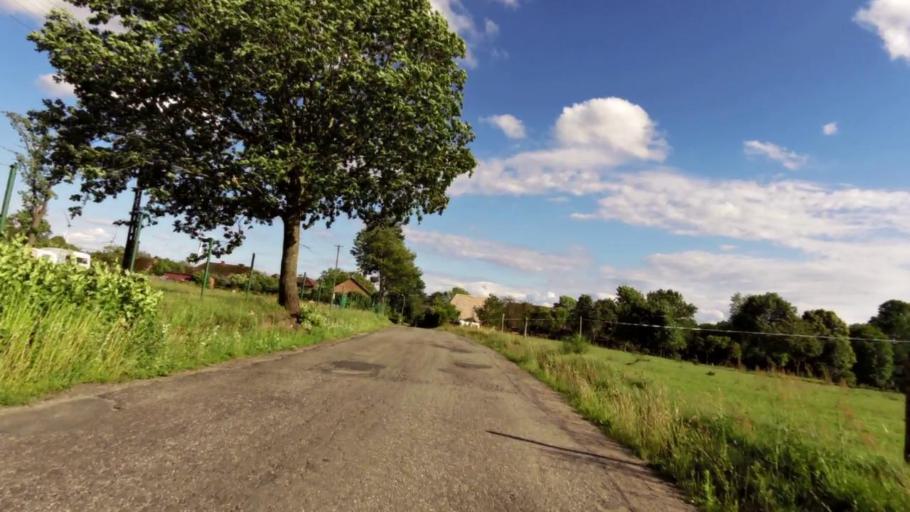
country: PL
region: West Pomeranian Voivodeship
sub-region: Powiat slawienski
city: Slawno
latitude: 54.4332
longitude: 16.7693
